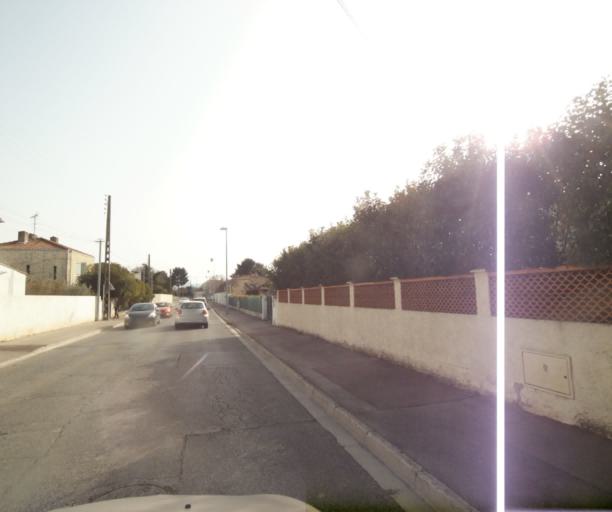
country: FR
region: Provence-Alpes-Cote d'Azur
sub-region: Departement des Bouches-du-Rhone
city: Vitrolles
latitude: 43.4557
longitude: 5.2427
